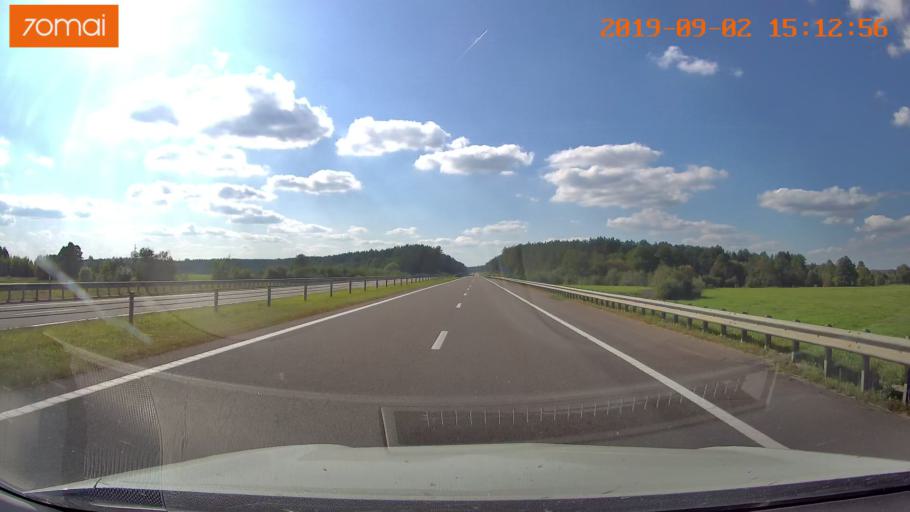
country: BY
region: Mogilev
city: Byalynichy
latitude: 53.9668
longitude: 29.7155
